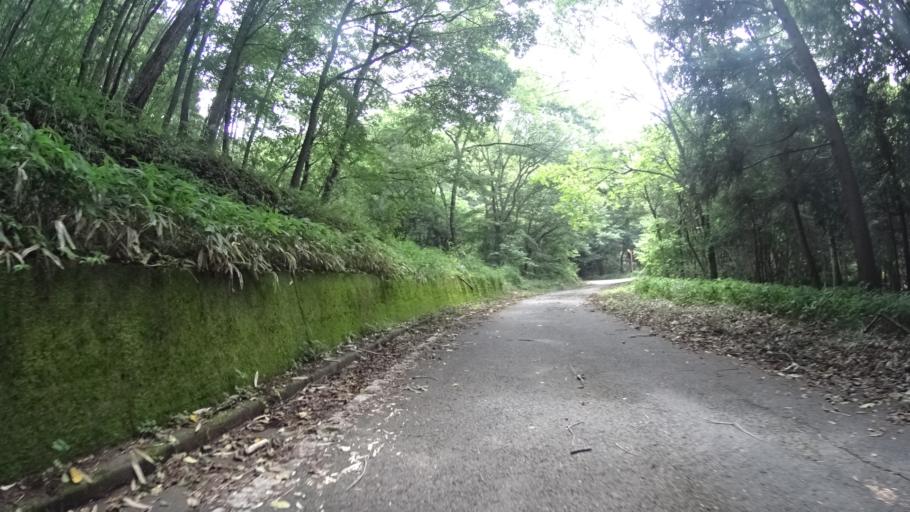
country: JP
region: Yamanashi
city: Nirasaki
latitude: 35.8810
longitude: 138.4841
